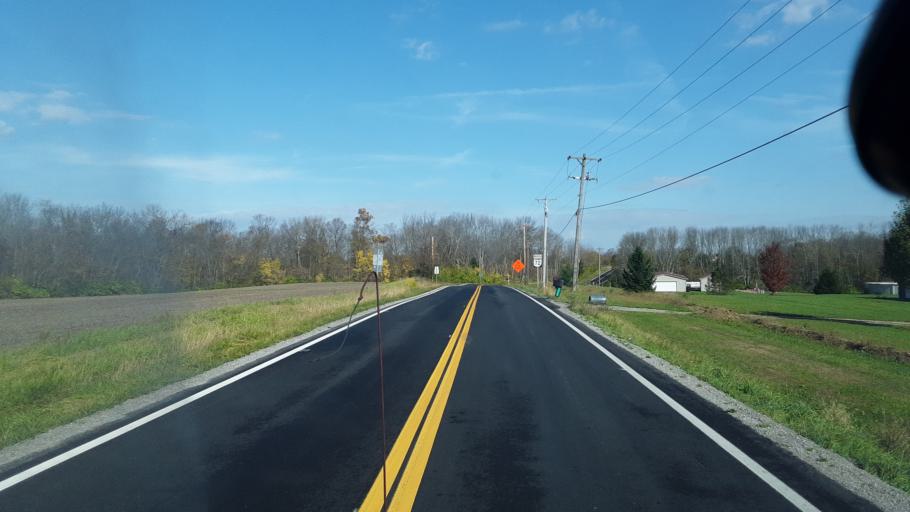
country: US
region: Ohio
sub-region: Highland County
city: Leesburg
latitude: 39.3472
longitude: -83.5881
